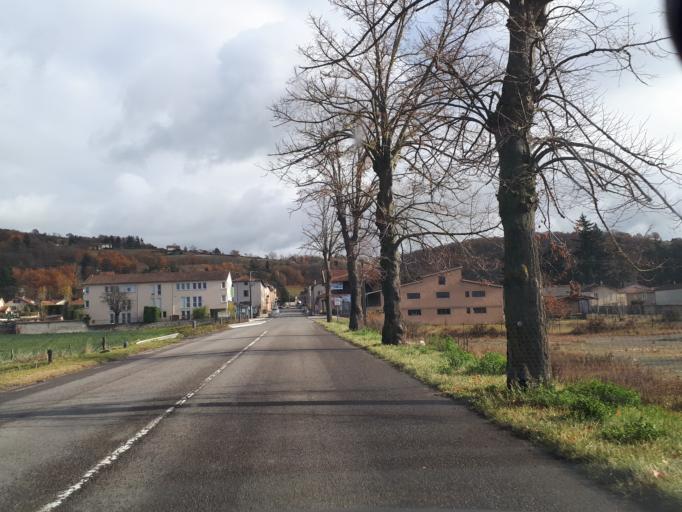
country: FR
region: Rhone-Alpes
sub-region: Departement de la Loire
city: Bellegarde-en-Forez
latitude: 45.6465
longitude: 4.2923
